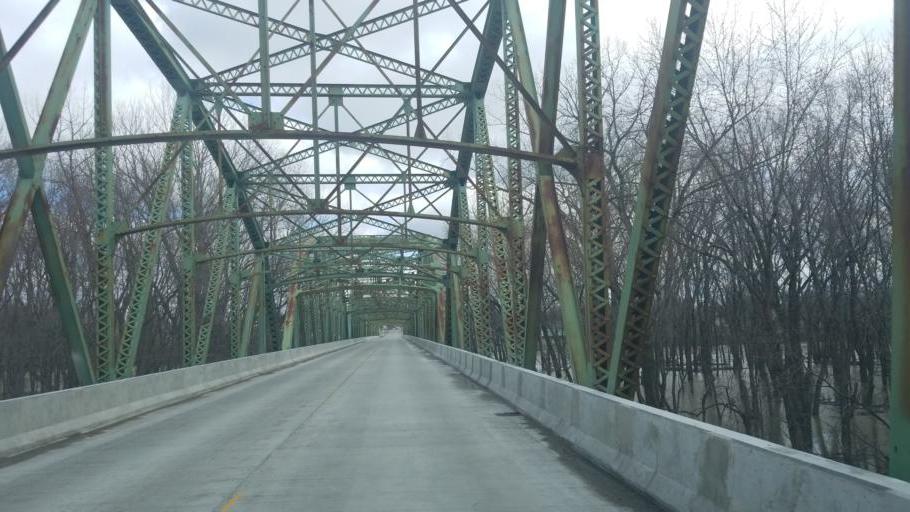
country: US
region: Indiana
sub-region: Parke County
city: Montezuma
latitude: 39.7921
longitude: -87.3773
